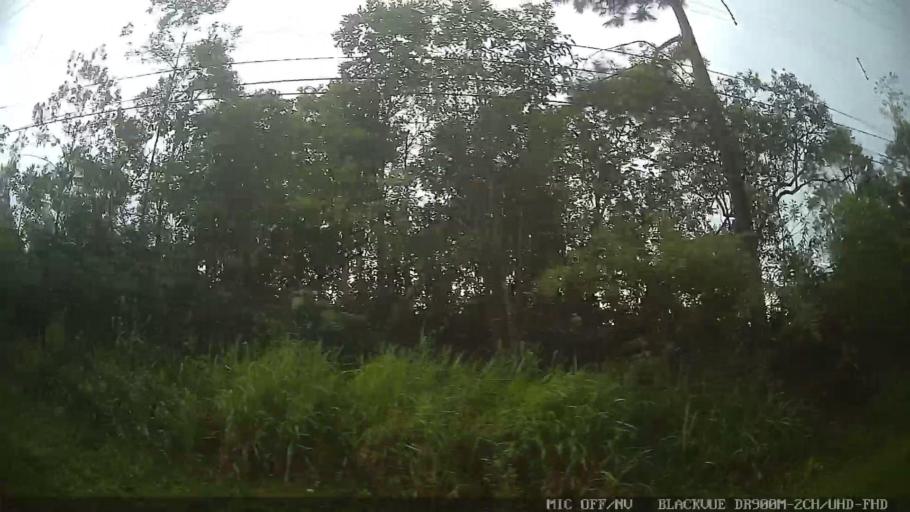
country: BR
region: Sao Paulo
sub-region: Ribeirao Pires
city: Ribeirao Pires
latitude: -23.6872
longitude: -46.3414
